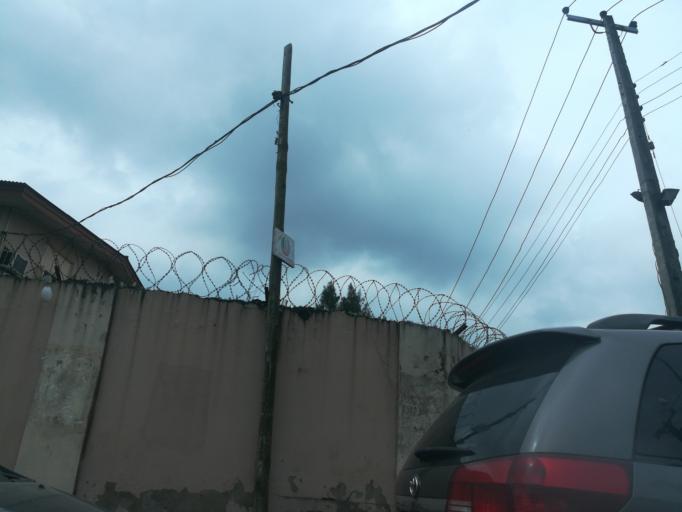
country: NG
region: Lagos
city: Ojota
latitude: 6.5695
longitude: 3.3658
